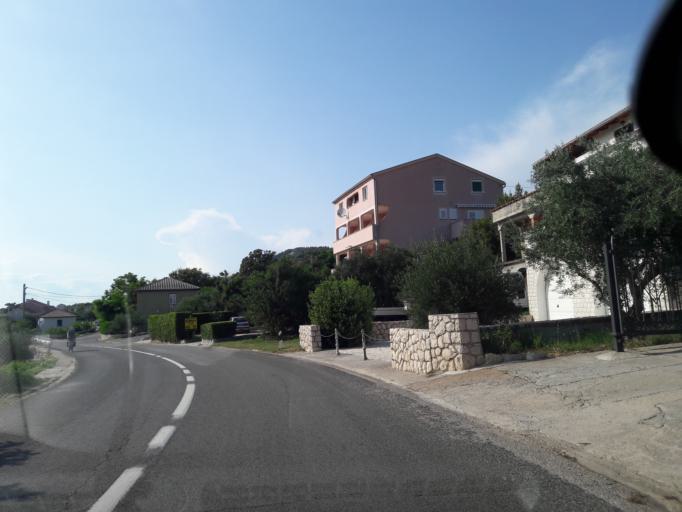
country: HR
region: Primorsko-Goranska
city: Banjol
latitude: 44.7296
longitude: 14.8144
